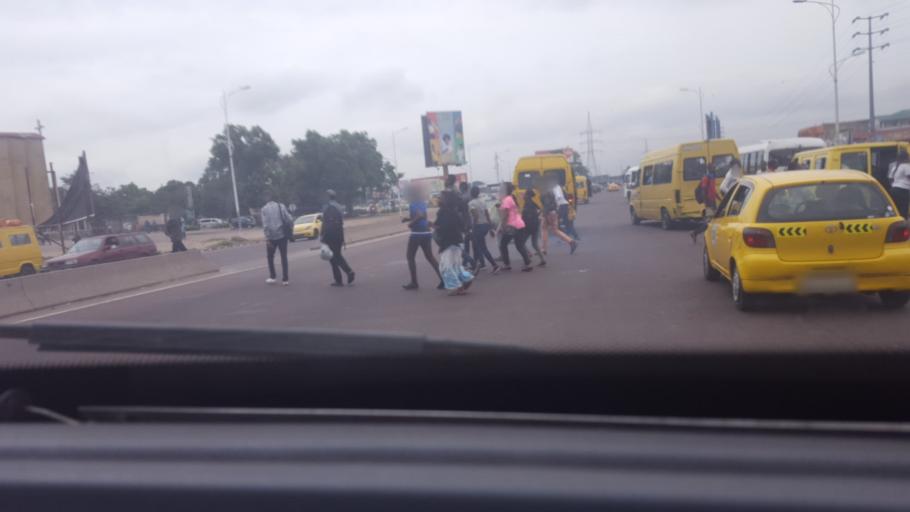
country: CD
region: Kinshasa
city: Kinshasa
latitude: -4.3379
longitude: 15.3280
